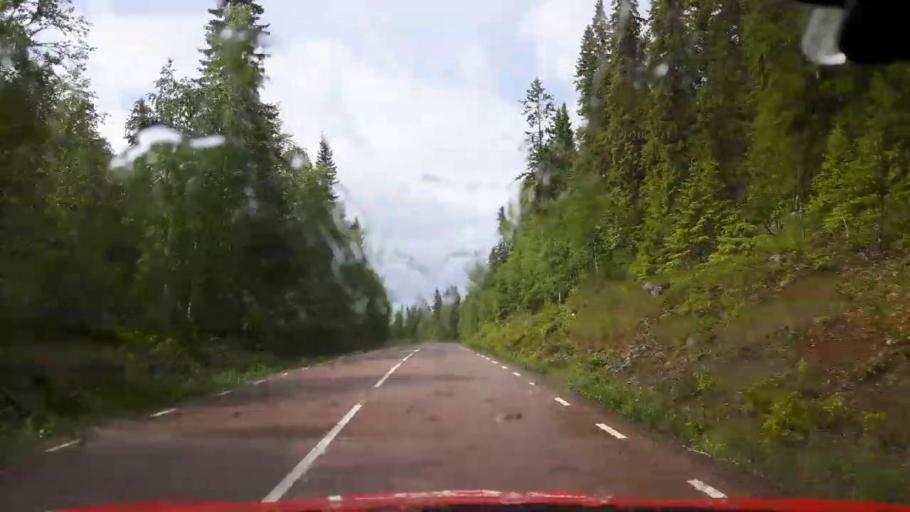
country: SE
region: Jaemtland
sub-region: Krokoms Kommun
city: Valla
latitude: 63.9522
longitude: 14.2103
